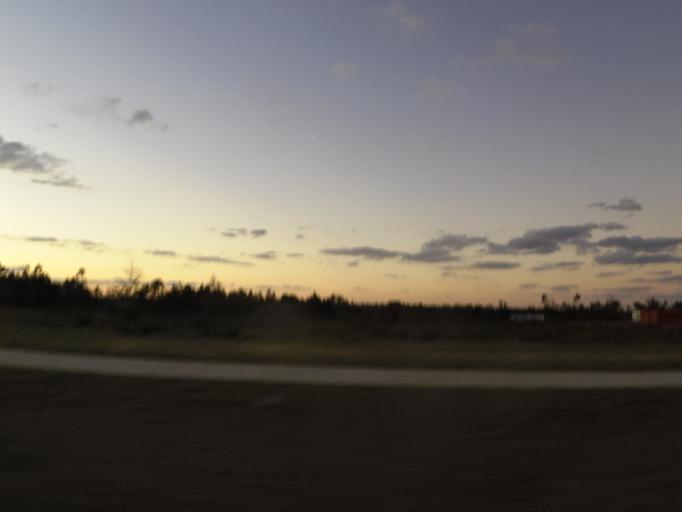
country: US
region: Florida
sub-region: Saint Johns County
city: Palm Valley
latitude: 30.0835
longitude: -81.4740
